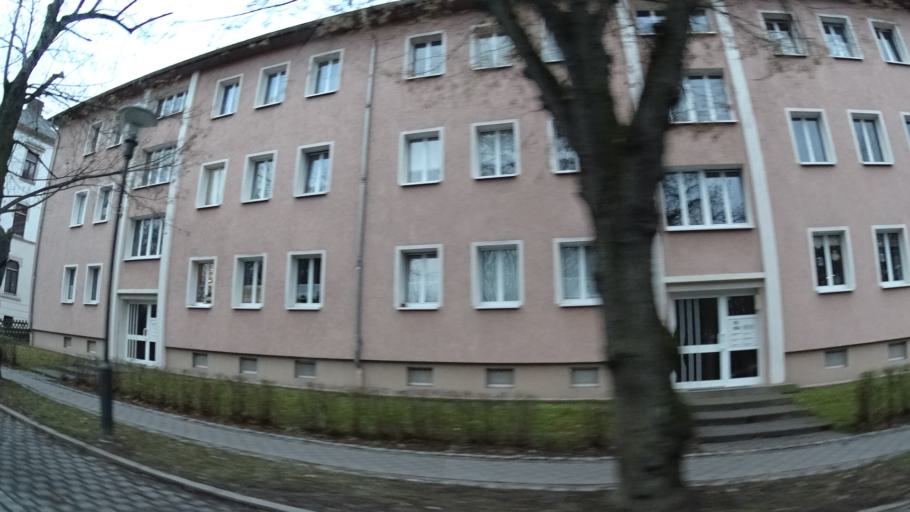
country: DE
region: Thuringia
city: Neustadt (Orla)
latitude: 50.7342
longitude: 11.7515
